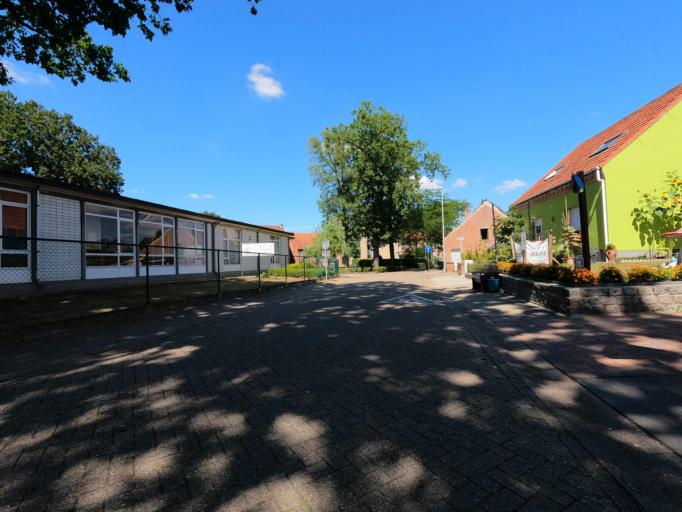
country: BE
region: Flanders
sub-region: Provincie Antwerpen
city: Kasterlee
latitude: 51.2372
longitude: 4.9649
